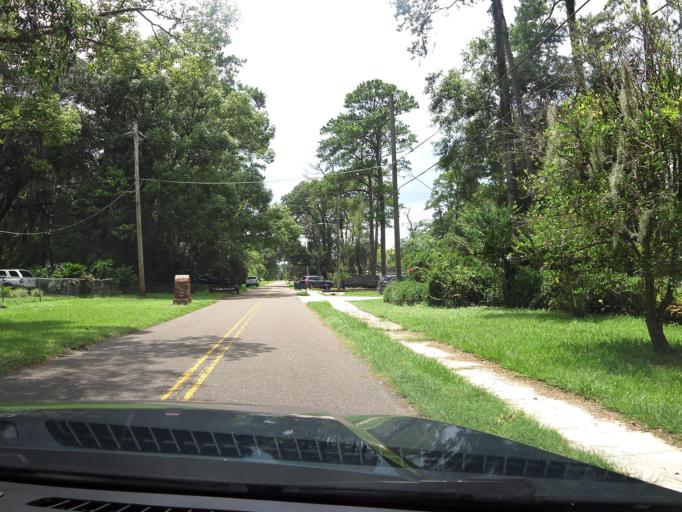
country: US
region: Florida
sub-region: Duval County
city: Jacksonville
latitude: 30.4239
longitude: -81.7068
